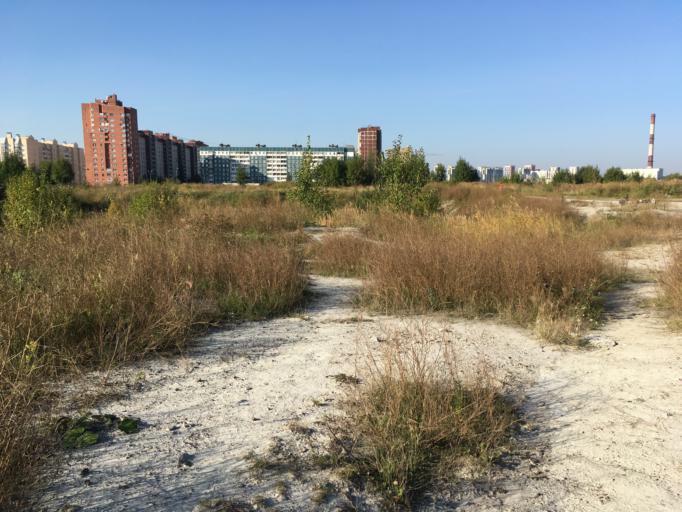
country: RU
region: St.-Petersburg
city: Komendantsky aerodrom
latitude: 60.0183
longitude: 30.2626
